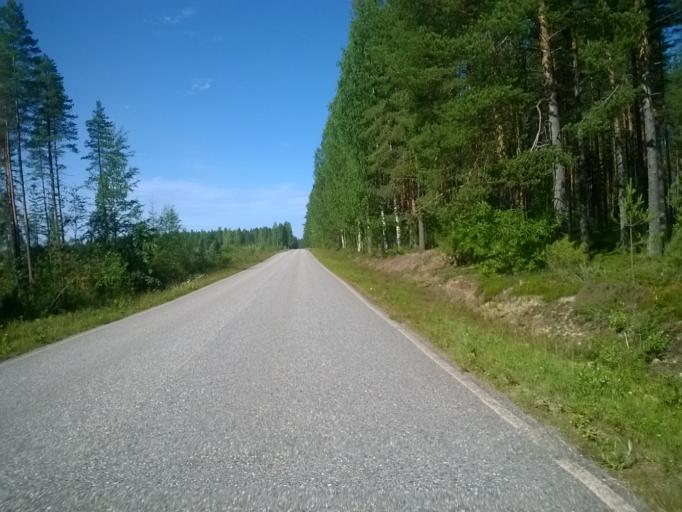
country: FI
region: Kainuu
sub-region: Kehys-Kainuu
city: Kuhmo
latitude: 64.1338
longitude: 29.4352
